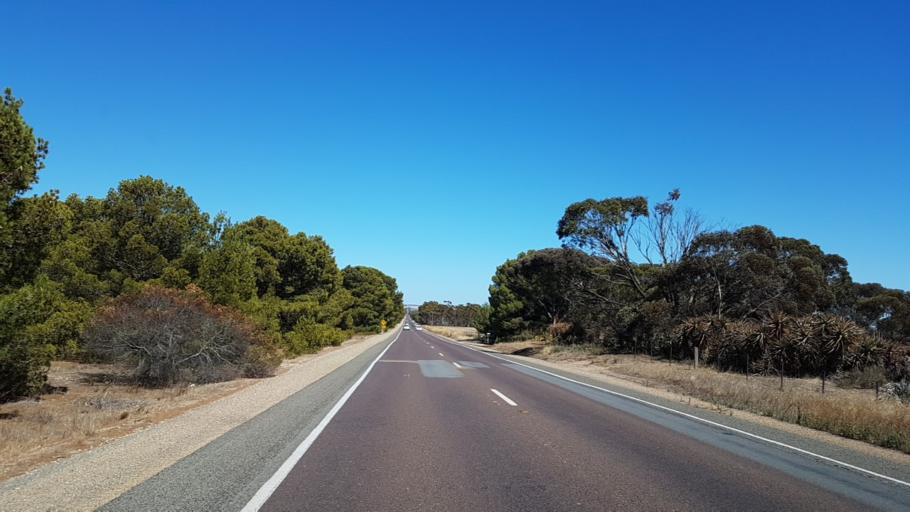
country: AU
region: South Australia
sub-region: Copper Coast
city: Kadina
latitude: -34.0583
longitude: 138.0285
